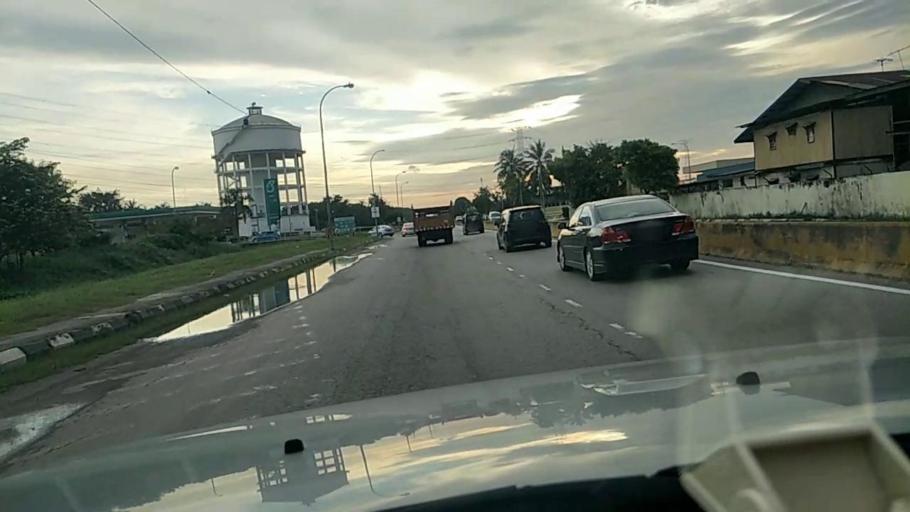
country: MY
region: Selangor
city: Klang
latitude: 3.1123
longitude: 101.4358
